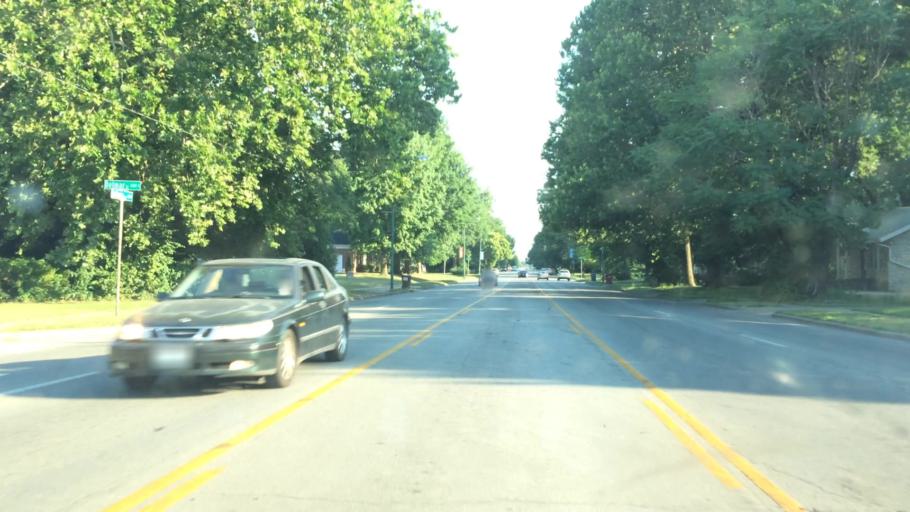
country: US
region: Missouri
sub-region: Greene County
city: Springfield
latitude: 37.1953
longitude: -93.2763
